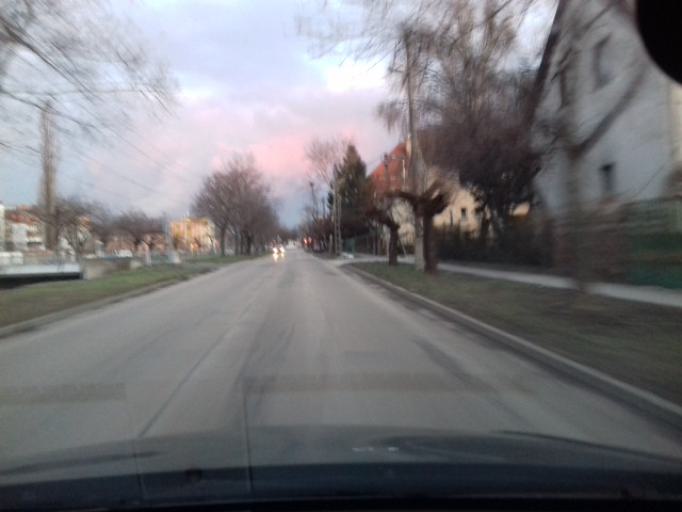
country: HU
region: Budapest
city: Budapest XIV. keruelet
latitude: 47.5263
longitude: 19.1130
